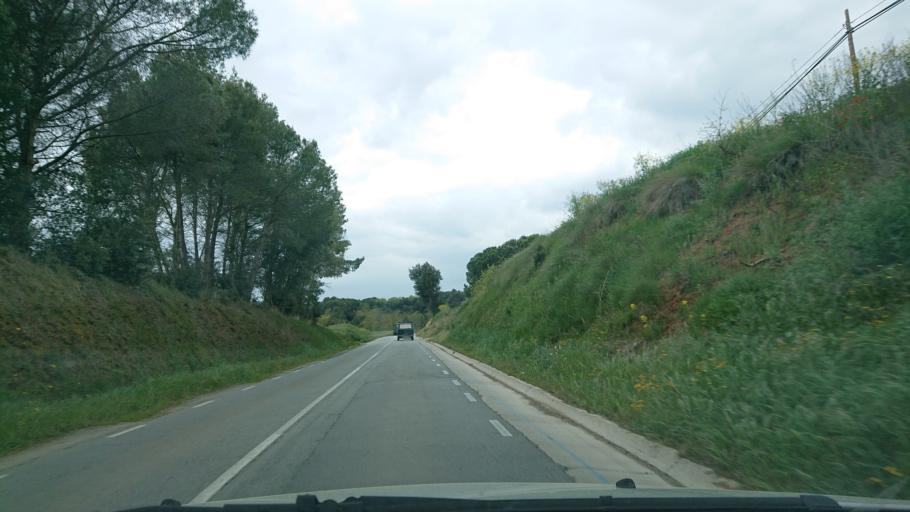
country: ES
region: Catalonia
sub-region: Provincia de Barcelona
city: Sant Pere de Vilamajor
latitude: 41.6766
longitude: 2.3815
